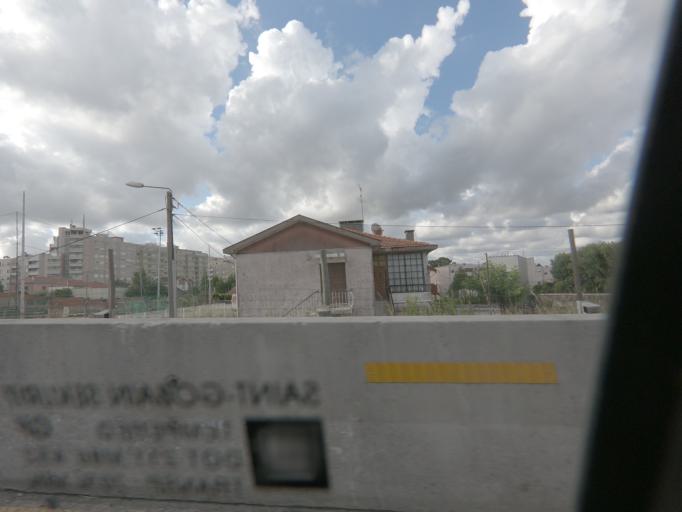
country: PT
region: Porto
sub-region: Gondomar
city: Rio Tinto
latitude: 41.2017
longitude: -8.5609
